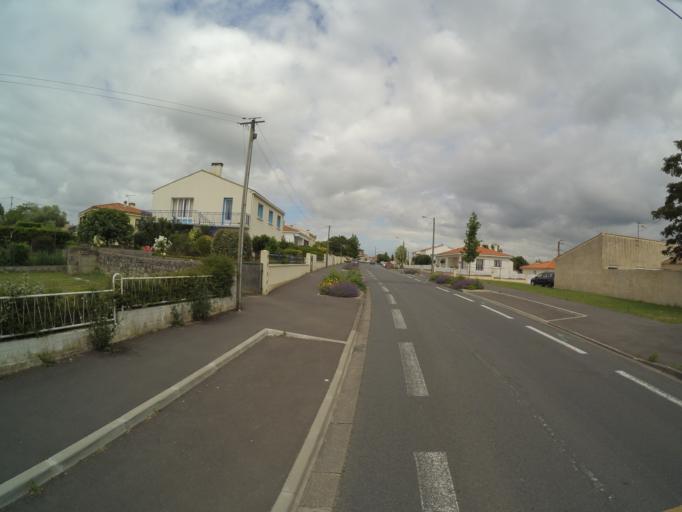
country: FR
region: Poitou-Charentes
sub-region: Departement de la Charente-Maritime
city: Rochefort
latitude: 45.9511
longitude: -0.9677
